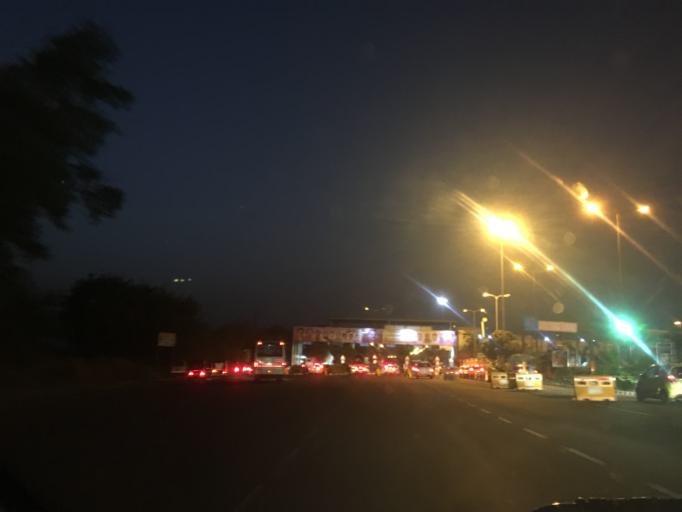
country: IN
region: Maharashtra
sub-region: Thane
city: Airoli
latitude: 19.1531
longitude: 72.9670
